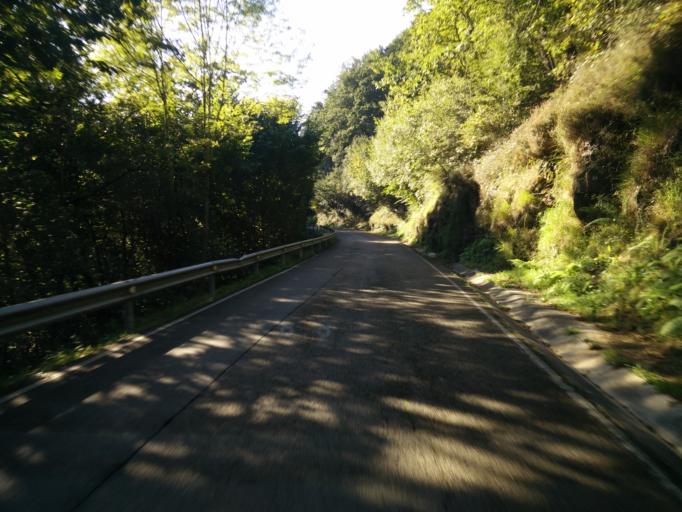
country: ES
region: Cantabria
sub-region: Provincia de Cantabria
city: San Pedro del Romeral
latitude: 43.1394
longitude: -3.8162
